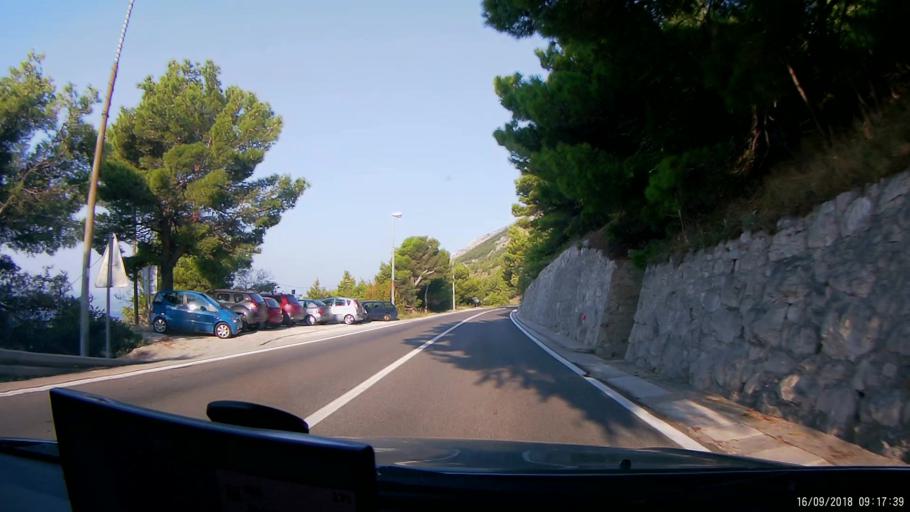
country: HR
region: Splitsko-Dalmatinska
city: Donja Brela
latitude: 43.4027
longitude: 16.8529
